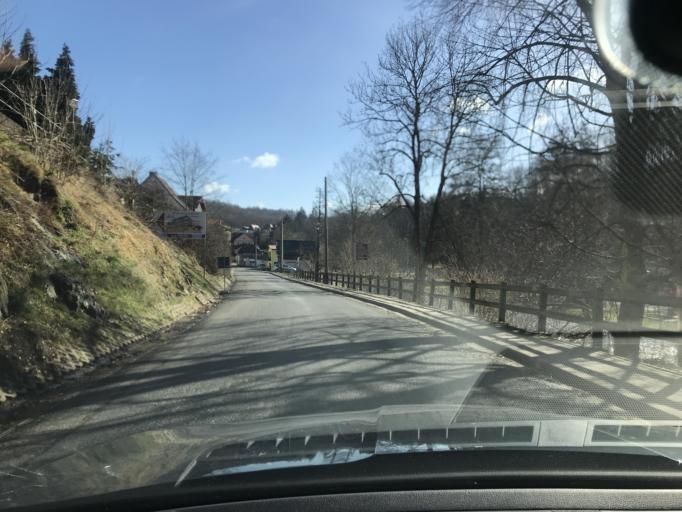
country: DE
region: Saxony-Anhalt
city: Huttenrode
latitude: 51.7268
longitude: 10.9391
